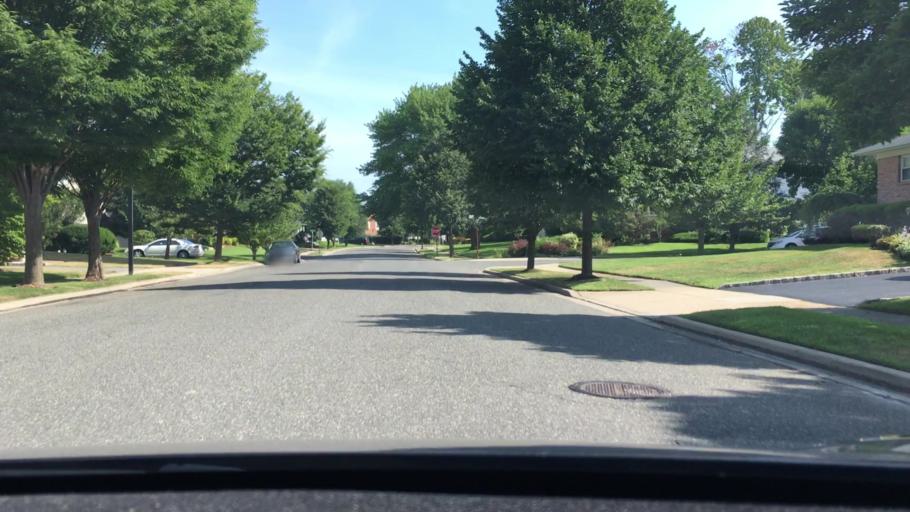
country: US
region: New York
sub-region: Nassau County
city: Jericho
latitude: 40.7930
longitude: -73.5204
